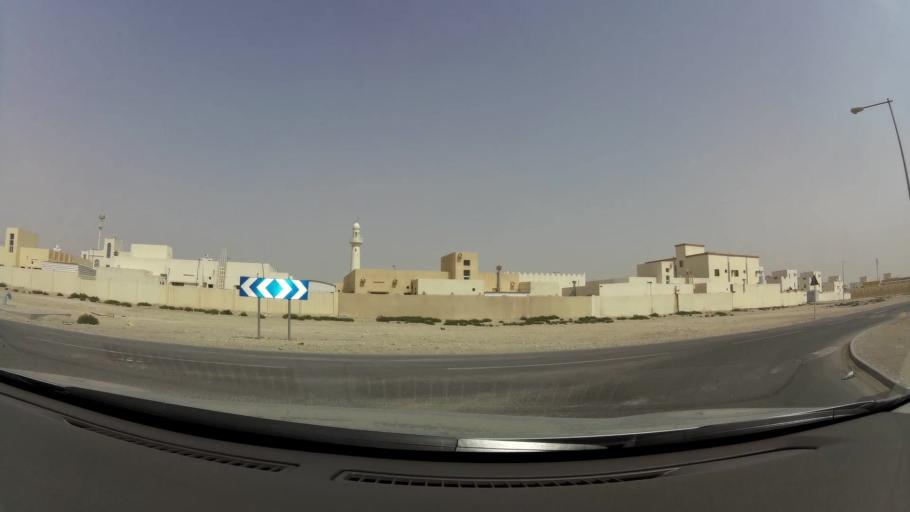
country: QA
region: Baladiyat ar Rayyan
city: Ar Rayyan
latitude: 25.2387
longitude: 51.3724
